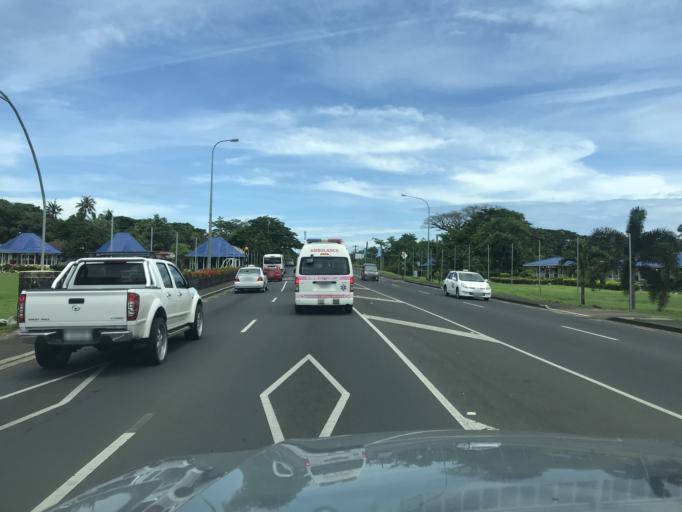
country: WS
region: Tuamasaga
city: Vaiusu
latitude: -13.8357
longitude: -171.7867
